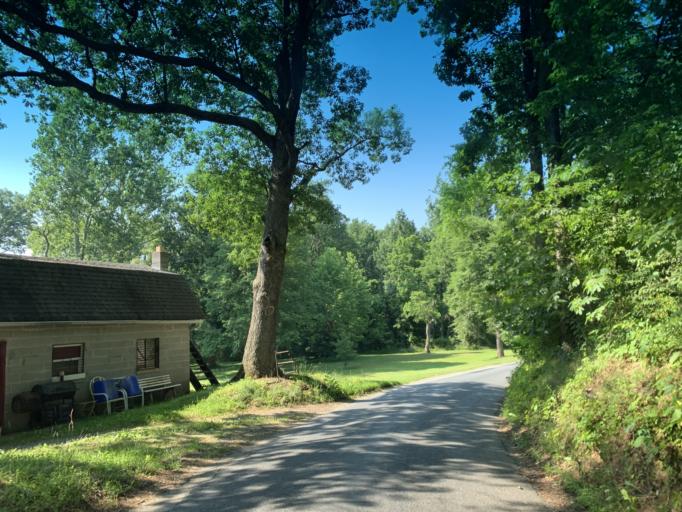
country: US
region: Maryland
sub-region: Montgomery County
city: Poolesville
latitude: 39.1482
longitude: -77.4542
